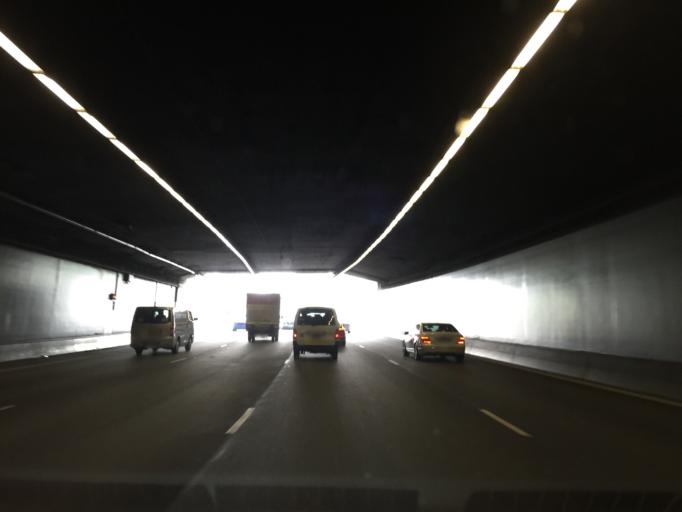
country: SG
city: Singapore
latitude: 1.3066
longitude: 103.8402
